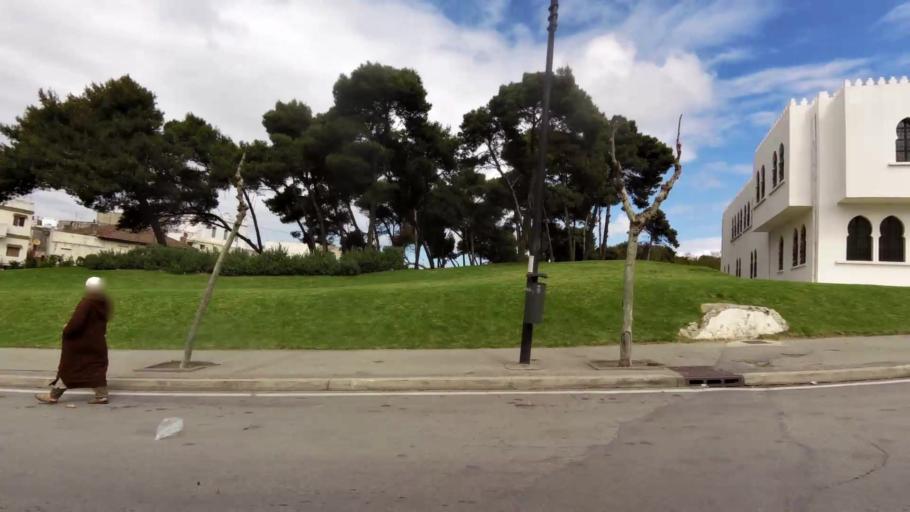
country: MA
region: Tanger-Tetouan
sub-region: Tanger-Assilah
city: Tangier
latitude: 35.7838
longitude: -5.8191
